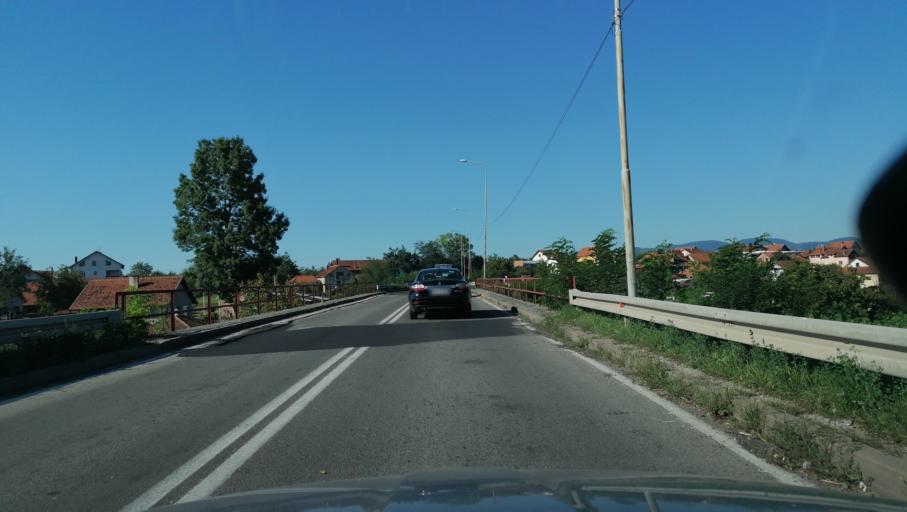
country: RS
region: Central Serbia
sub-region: Raski Okrug
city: Kraljevo
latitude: 43.7258
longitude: 20.6483
